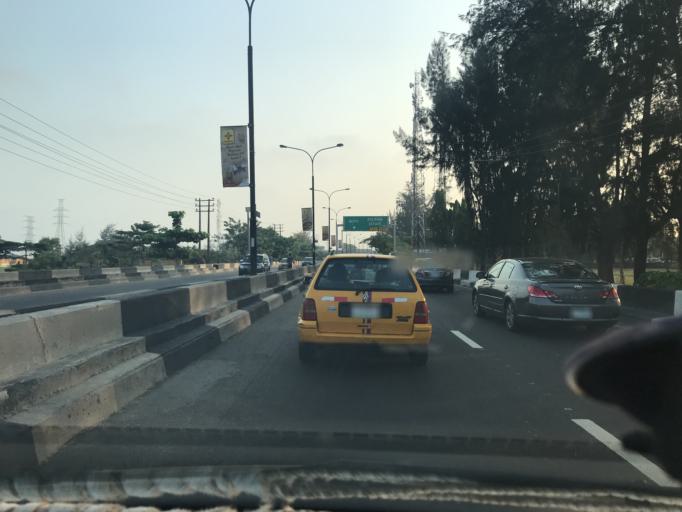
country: NG
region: Lagos
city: Lagos
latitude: 6.4606
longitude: 3.4147
